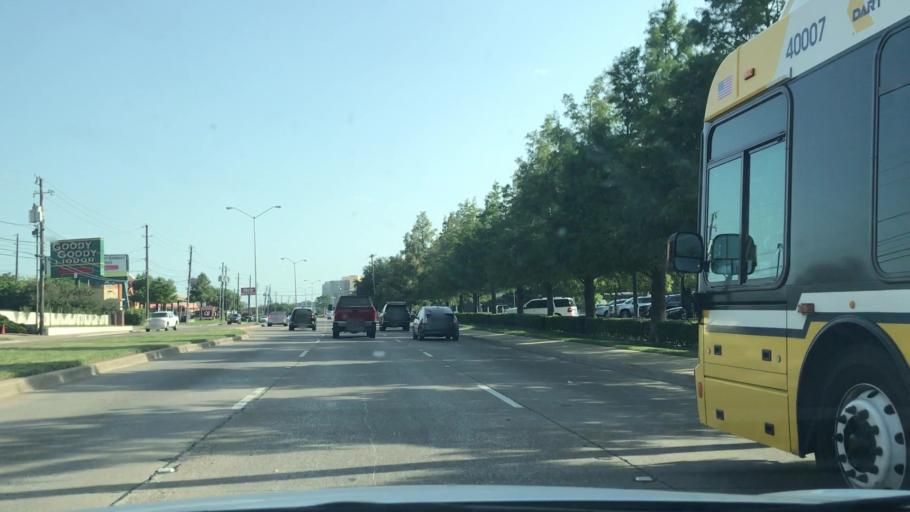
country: US
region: Texas
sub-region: Dallas County
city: University Park
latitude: 32.8772
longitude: -96.7613
